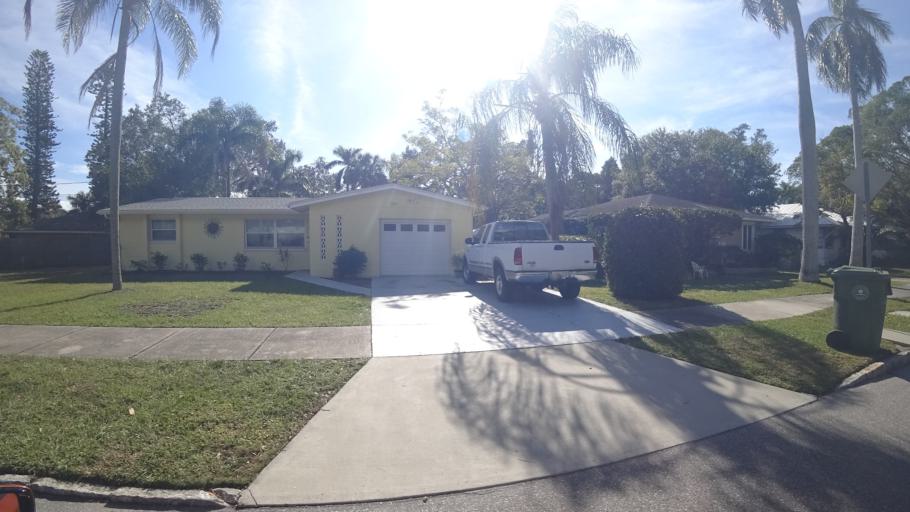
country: US
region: Florida
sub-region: Manatee County
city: Bradenton
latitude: 27.4937
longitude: -82.5804
